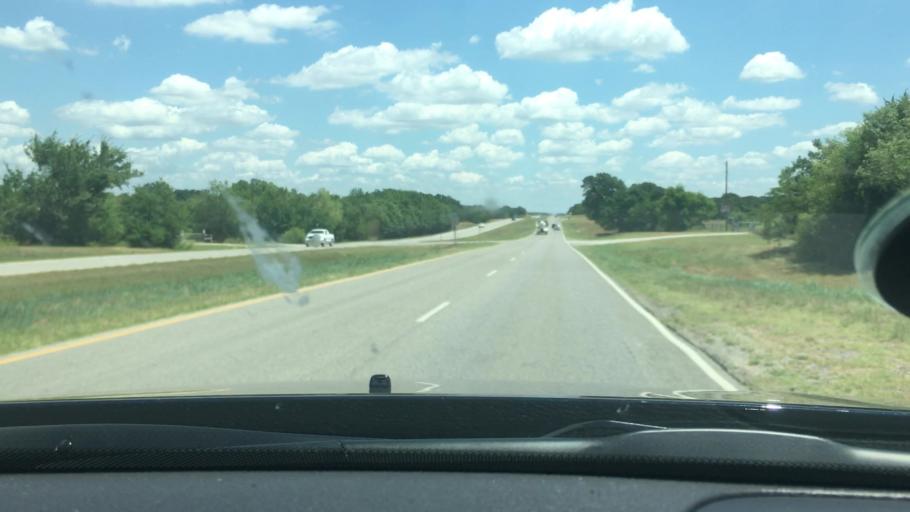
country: US
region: Oklahoma
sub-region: Carter County
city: Wilson
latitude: 34.1728
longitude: -97.4014
